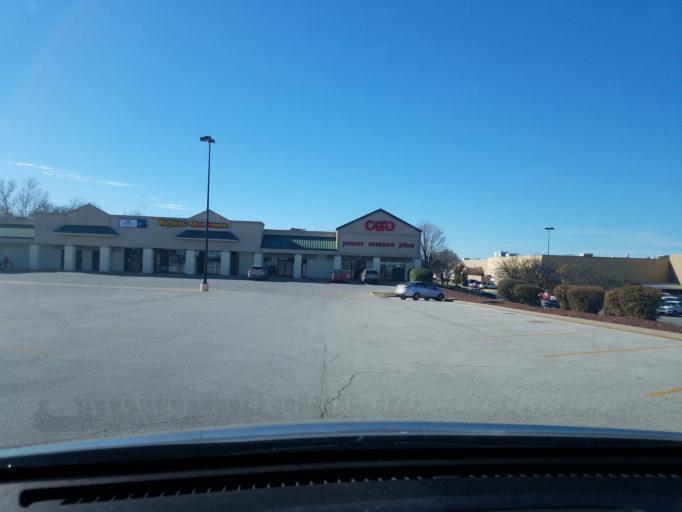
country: US
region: Arkansas
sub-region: Carroll County
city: Berryville
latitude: 36.3768
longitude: -93.5850
